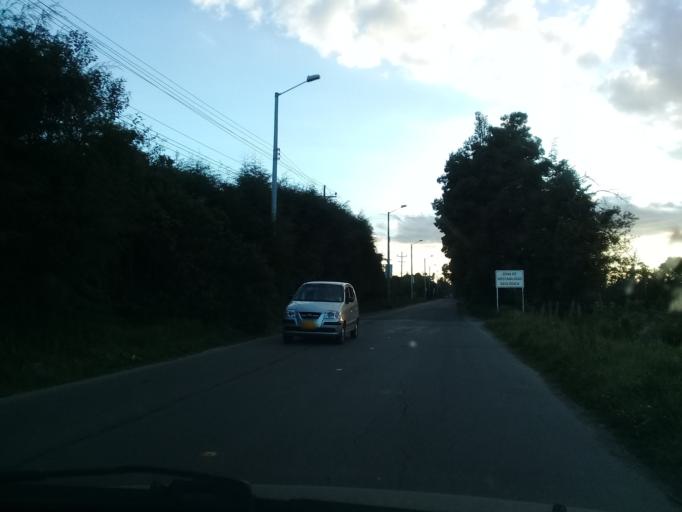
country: CO
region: Cundinamarca
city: Cota
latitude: 4.7907
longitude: -74.1532
